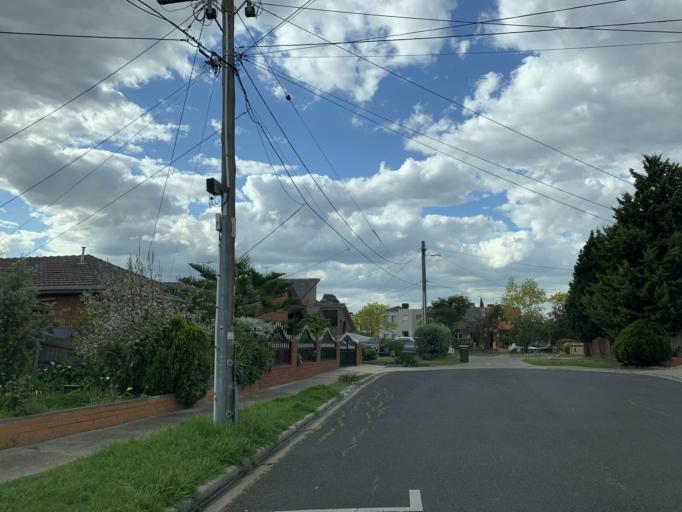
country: AU
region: Victoria
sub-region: Moonee Valley
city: Keilor East
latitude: -37.7509
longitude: 144.8522
